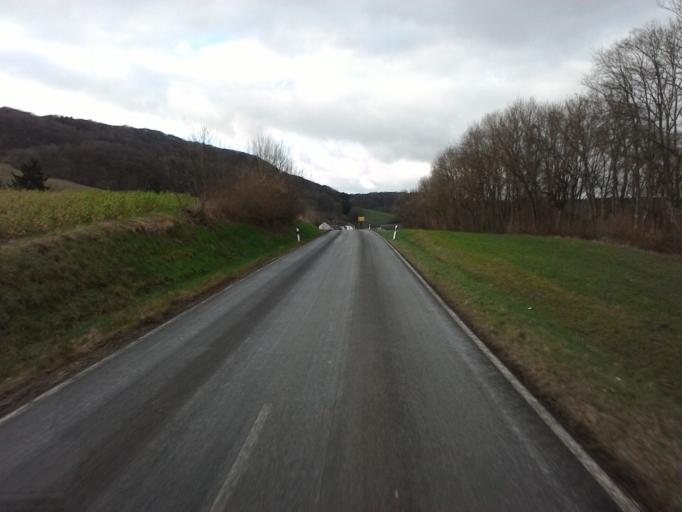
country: DE
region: Rheinland-Pfalz
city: Peffingen
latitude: 49.9052
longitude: 6.4077
